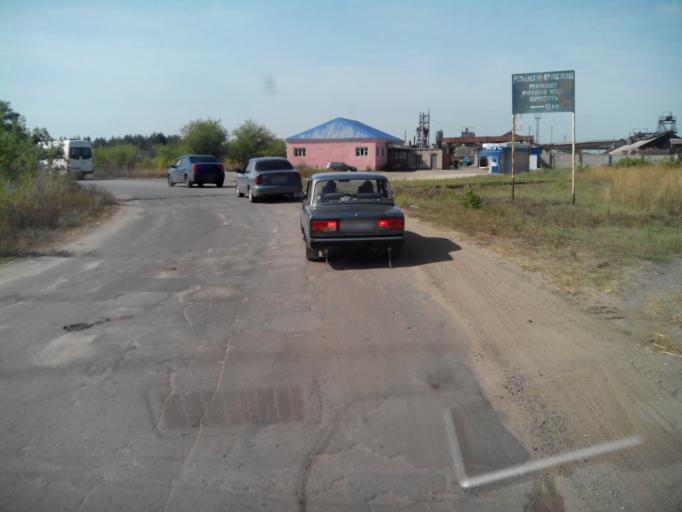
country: RU
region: Samara
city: Balasheyka
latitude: 53.1693
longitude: 48.1383
